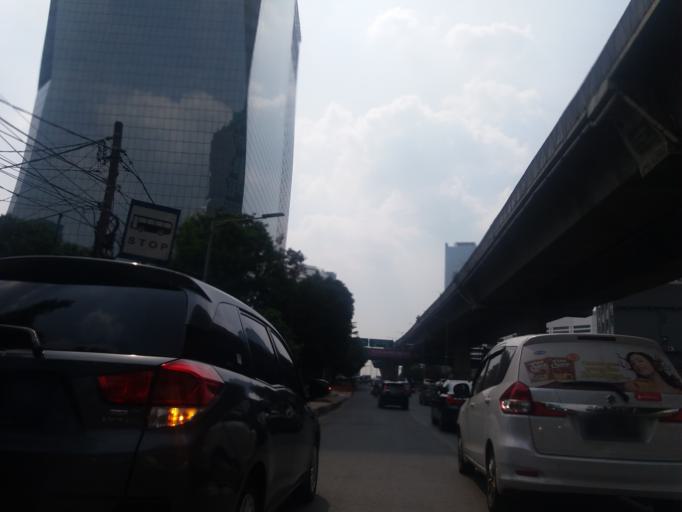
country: ID
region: Jakarta Raya
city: Jakarta
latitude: -6.2187
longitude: 106.8195
